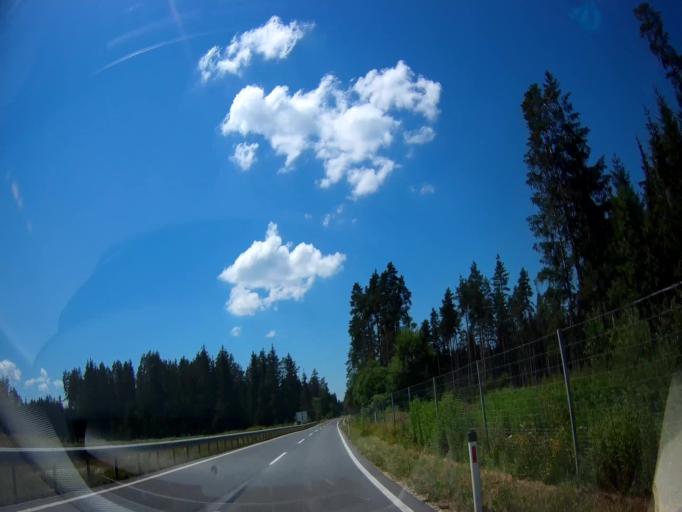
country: AT
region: Carinthia
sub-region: Politischer Bezirk Volkermarkt
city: Bleiburg/Pliberk
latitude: 46.6023
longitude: 14.7568
